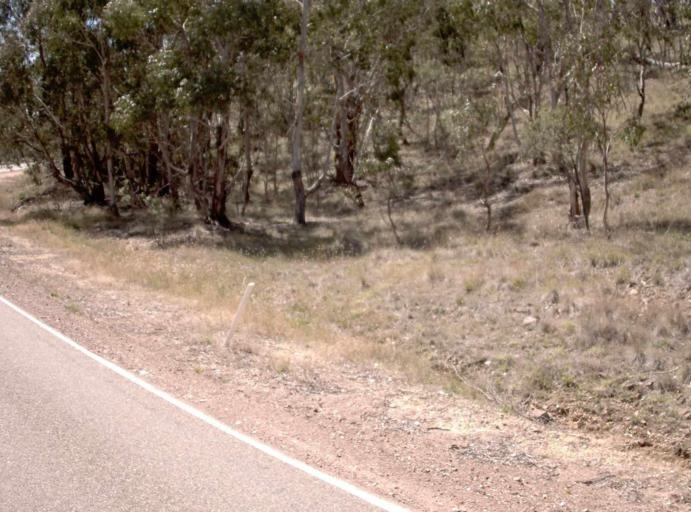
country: AU
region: Victoria
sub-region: Alpine
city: Mount Beauty
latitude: -37.0420
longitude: 147.6238
